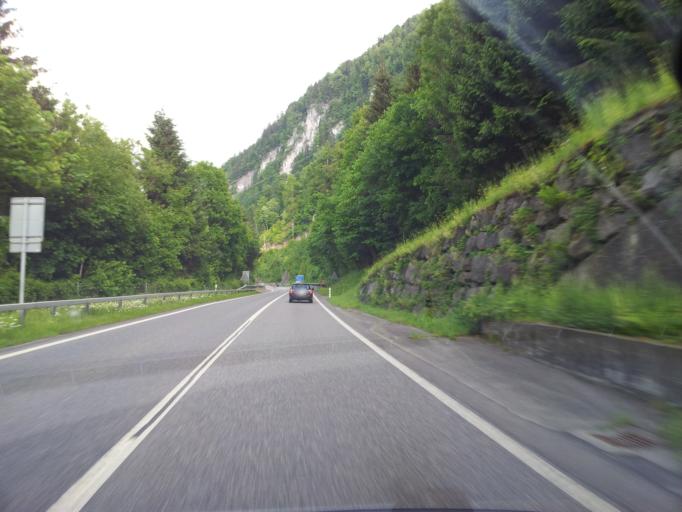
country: CH
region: Bern
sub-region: Interlaken-Oberhasli District
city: Brienz
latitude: 46.7393
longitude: 8.0414
